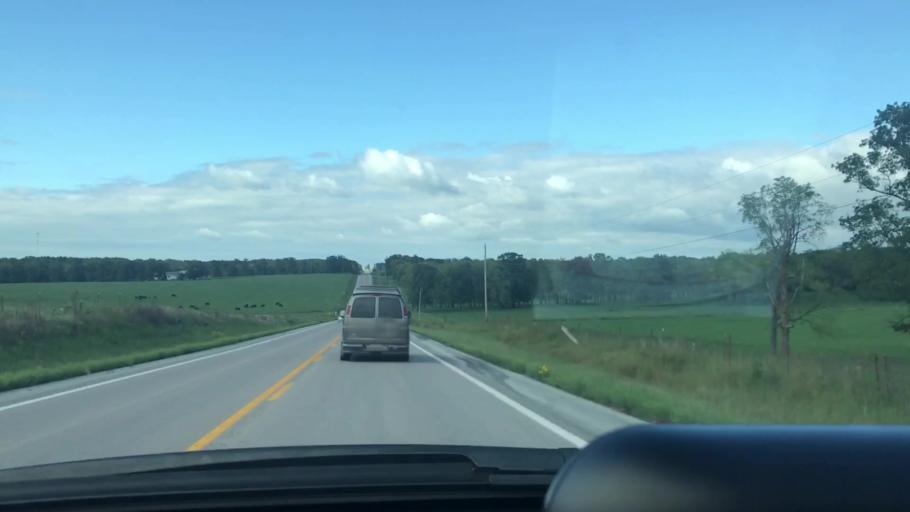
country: US
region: Missouri
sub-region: Hickory County
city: Hermitage
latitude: 37.9681
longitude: -93.2059
